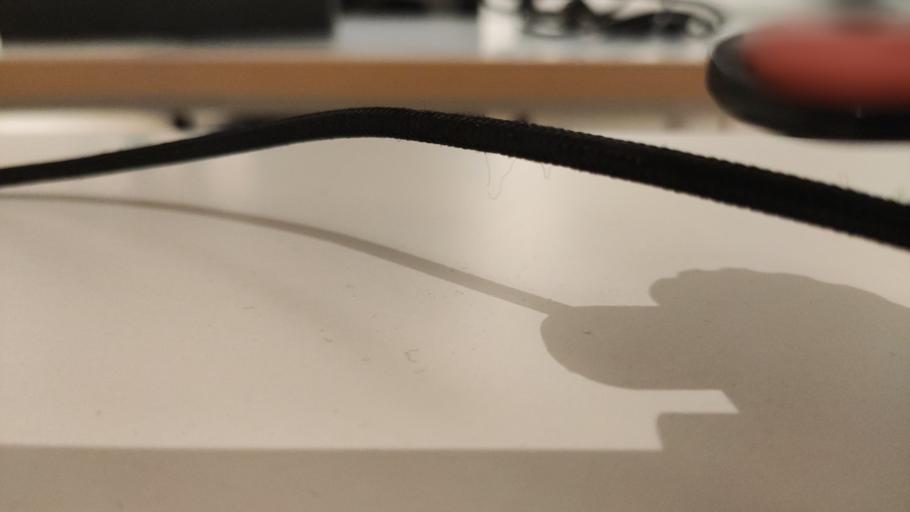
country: RU
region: Moskovskaya
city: Dorokhovo
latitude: 55.4091
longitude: 36.3733
